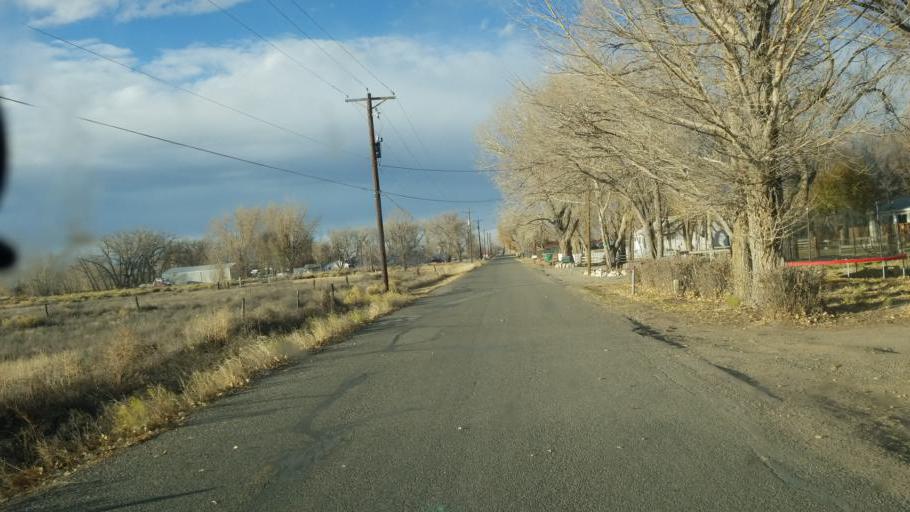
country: US
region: Colorado
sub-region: Alamosa County
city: Alamosa East
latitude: 37.4699
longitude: -105.8481
